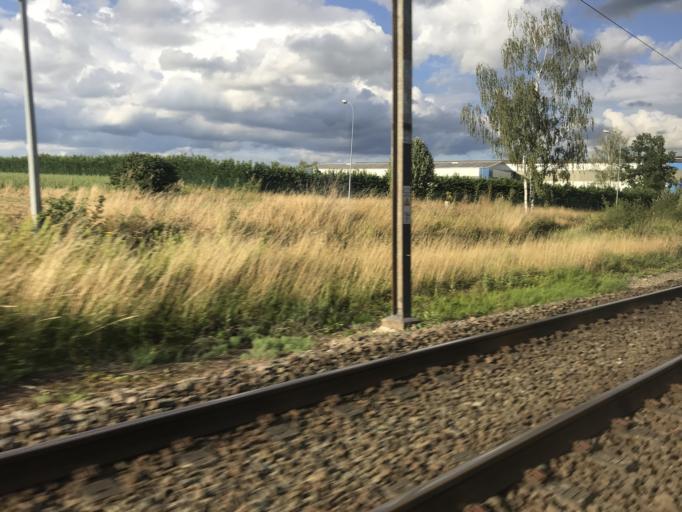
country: FR
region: Champagne-Ardenne
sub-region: Departement des Ardennes
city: Bazeilles
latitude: 49.6725
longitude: 4.9925
